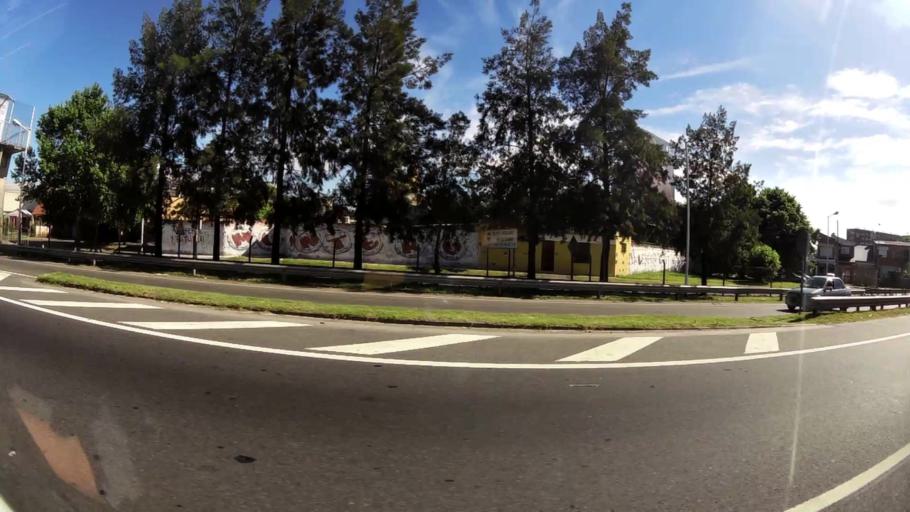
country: AR
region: Buenos Aires
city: Caseros
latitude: -34.6310
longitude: -58.5801
